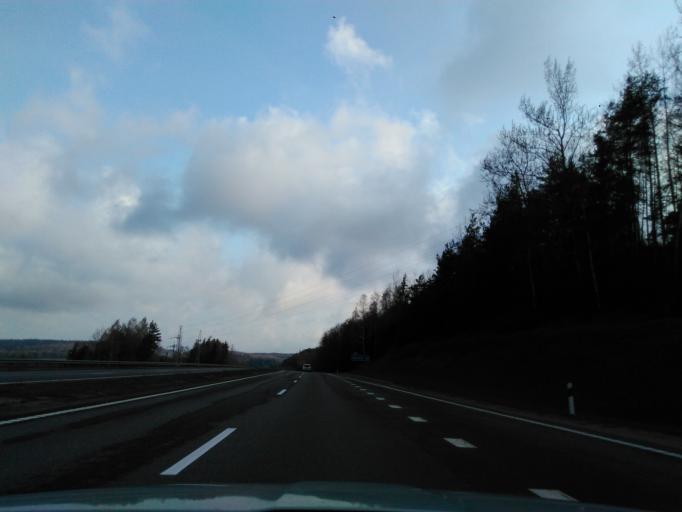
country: BY
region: Minsk
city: Lahoysk
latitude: 54.2010
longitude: 27.8174
